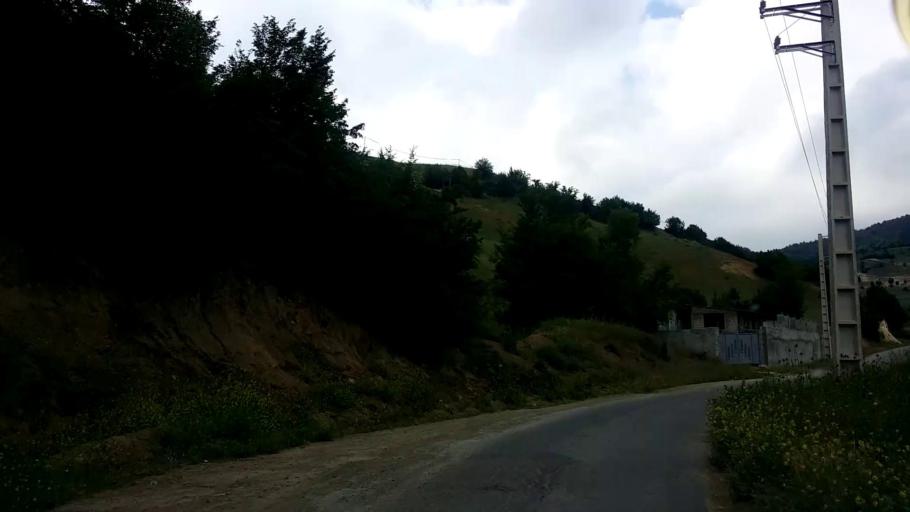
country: IR
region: Mazandaran
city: Chalus
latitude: 36.5496
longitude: 51.2700
